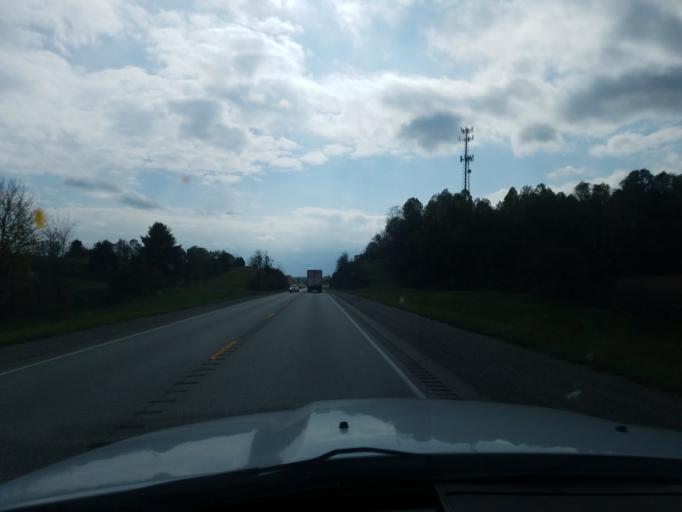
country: US
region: Kentucky
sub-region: Taylor County
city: Campbellsville
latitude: 37.4244
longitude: -85.2820
